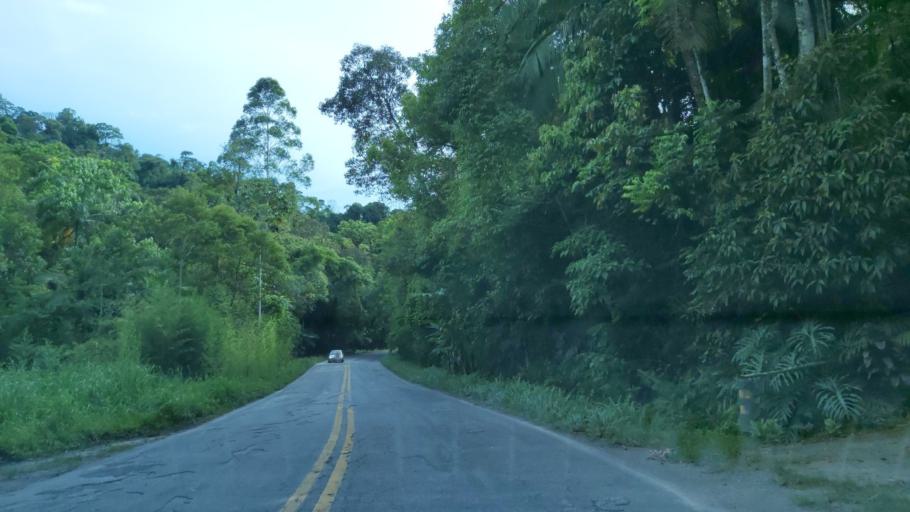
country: BR
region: Sao Paulo
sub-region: Miracatu
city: Miracatu
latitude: -24.0547
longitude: -47.5805
